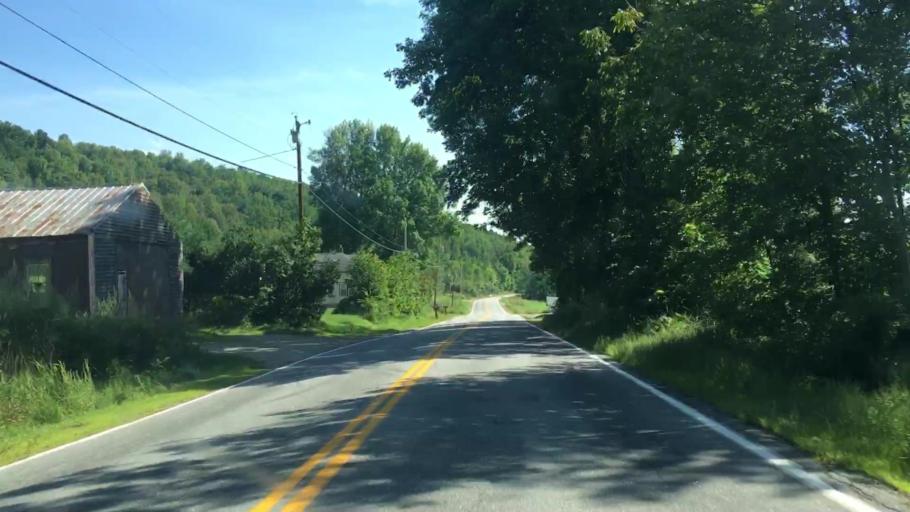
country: US
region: Maine
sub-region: Androscoggin County
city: Sabattus
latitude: 44.1395
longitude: -70.0876
